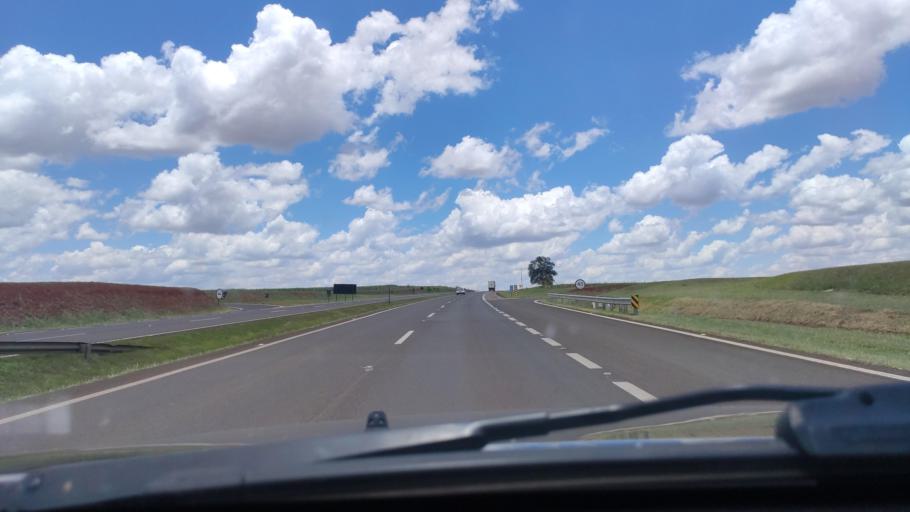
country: BR
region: Sao Paulo
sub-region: Pederneiras
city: Pederneiras
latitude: -22.3263
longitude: -48.7376
